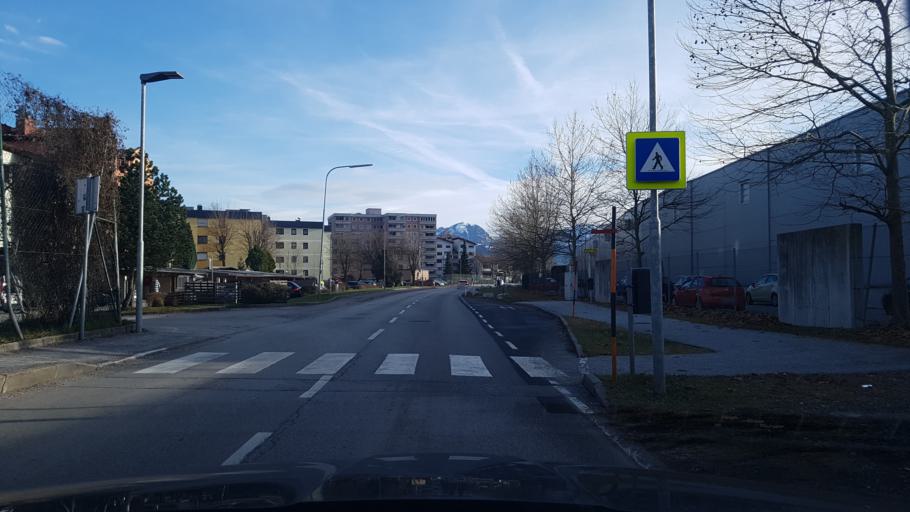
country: AT
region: Salzburg
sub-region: Politischer Bezirk Hallein
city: Hallein
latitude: 47.6798
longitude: 13.1113
